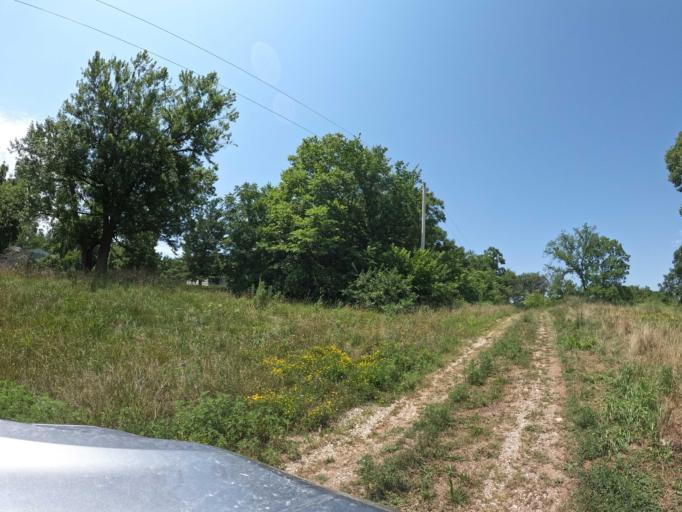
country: US
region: Iowa
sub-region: Appanoose County
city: Centerville
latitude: 40.7744
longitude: -92.9512
